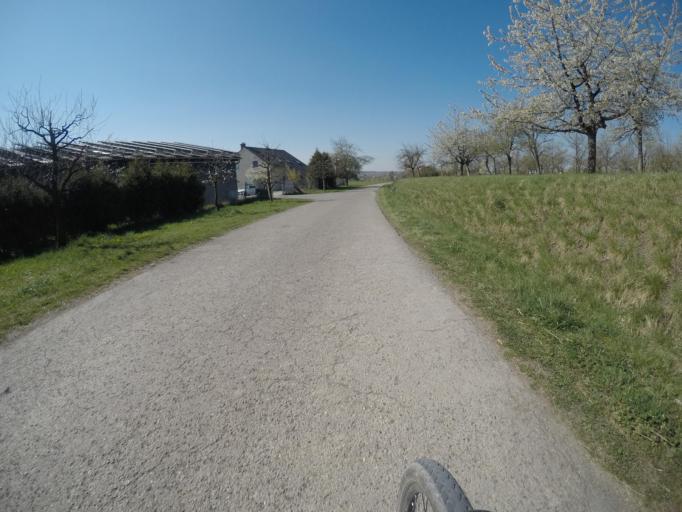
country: DE
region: Baden-Wuerttemberg
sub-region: Regierungsbezirk Stuttgart
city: Herrenberg
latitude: 48.5658
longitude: 8.9226
